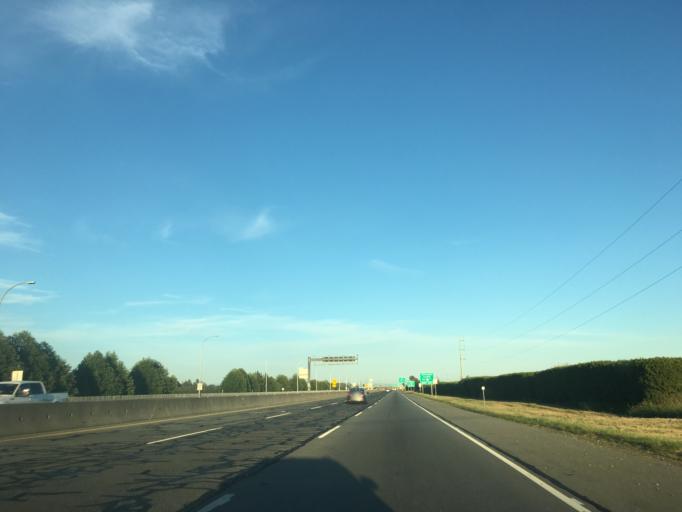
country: CA
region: British Columbia
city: Ladner
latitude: 49.1034
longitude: -123.0462
